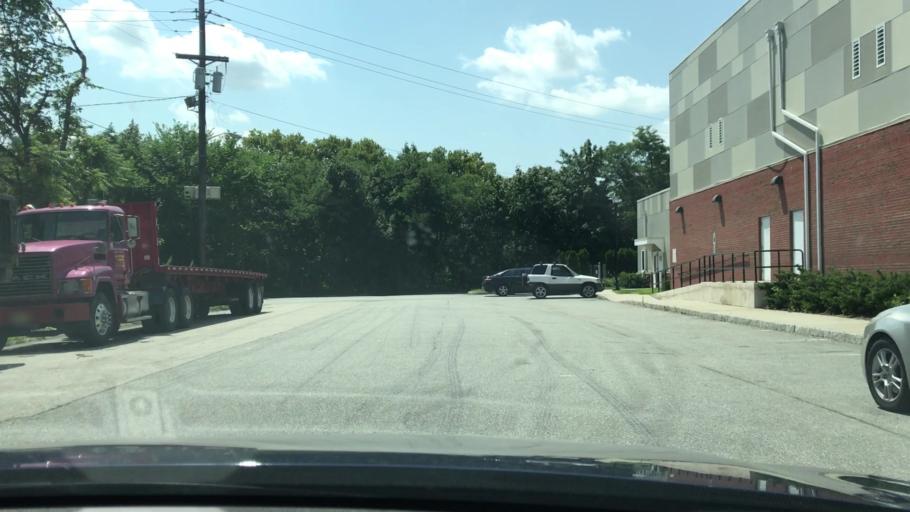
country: US
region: New Jersey
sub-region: Bergen County
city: Elmwood Park
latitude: 40.9015
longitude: -74.1435
